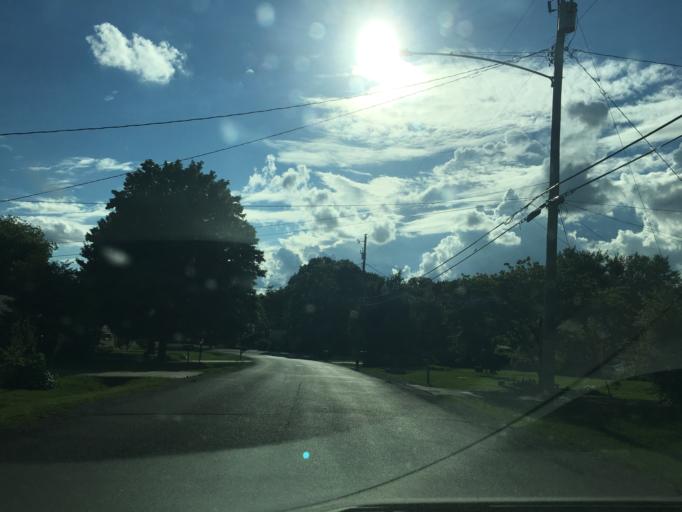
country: US
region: Tennessee
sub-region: Davidson County
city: Oak Hill
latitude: 36.0967
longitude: -86.7318
